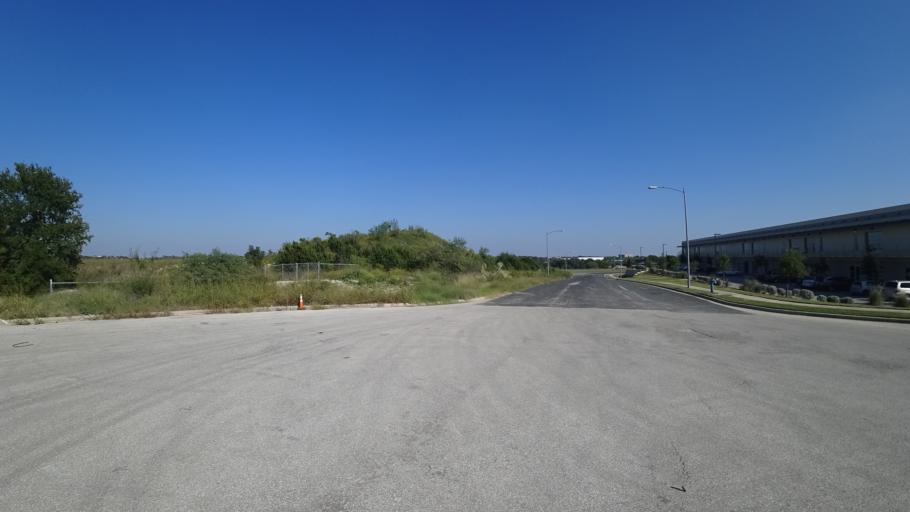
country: US
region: Texas
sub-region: Travis County
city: Austin
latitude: 30.3447
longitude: -97.6853
